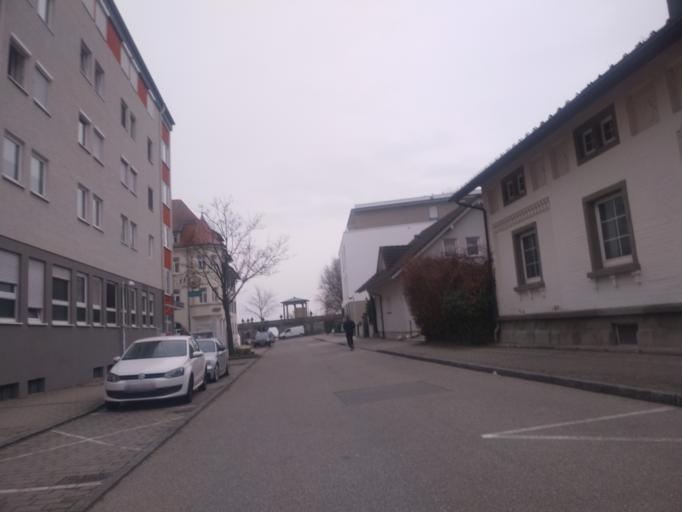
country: DE
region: Baden-Wuerttemberg
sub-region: Tuebingen Region
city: Friedrichshafen
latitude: 47.6505
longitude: 9.4676
